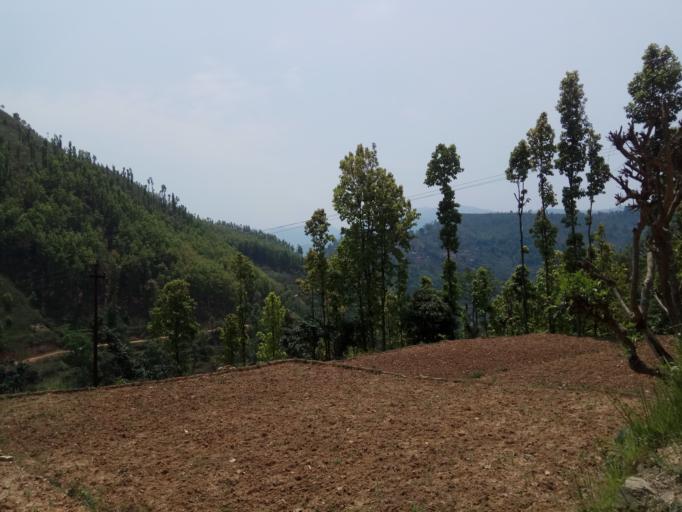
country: NP
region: Central Region
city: Kirtipur
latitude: 27.8961
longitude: 85.0859
